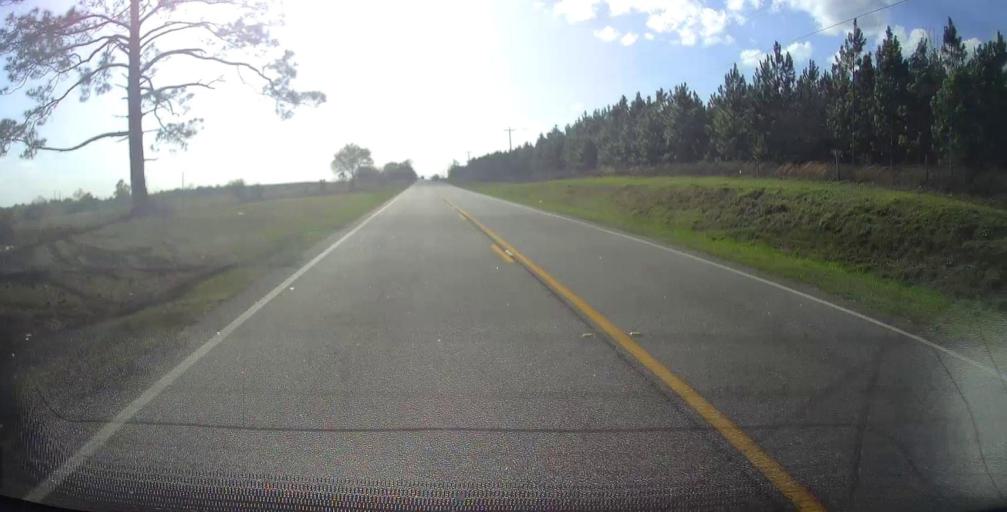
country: US
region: Georgia
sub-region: Wheeler County
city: Alamo
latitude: 32.1640
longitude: -82.7197
